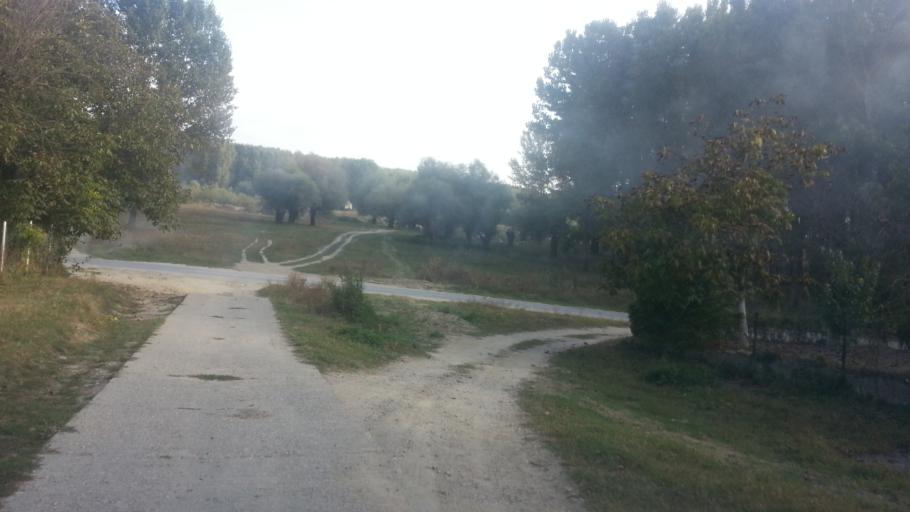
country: RS
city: Belegis
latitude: 45.0179
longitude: 20.3415
